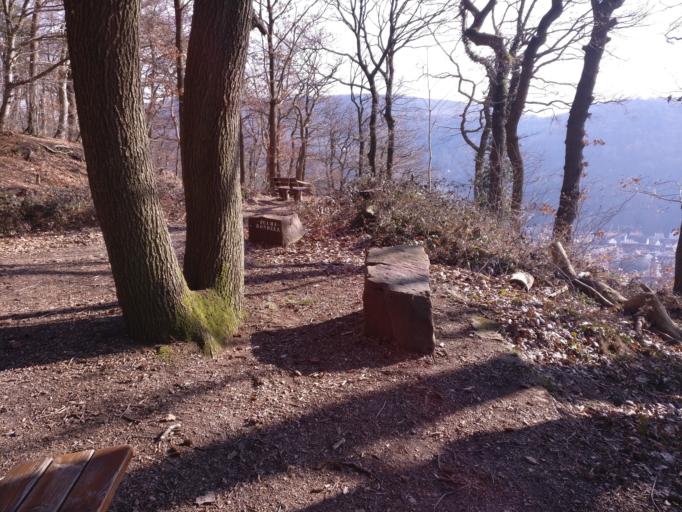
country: DE
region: Baden-Wuerttemberg
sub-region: Karlsruhe Region
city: Heidelberg
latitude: 49.4179
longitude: 8.7006
